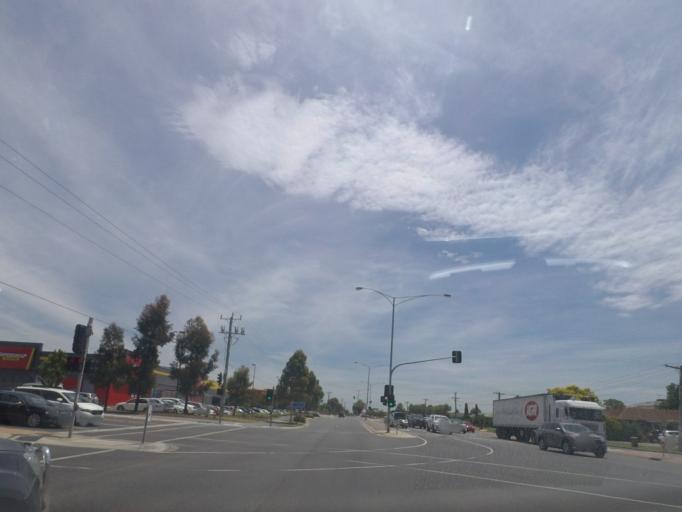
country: AU
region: Victoria
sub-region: Wyndham
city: Tarneit
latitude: -37.8750
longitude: 144.6832
